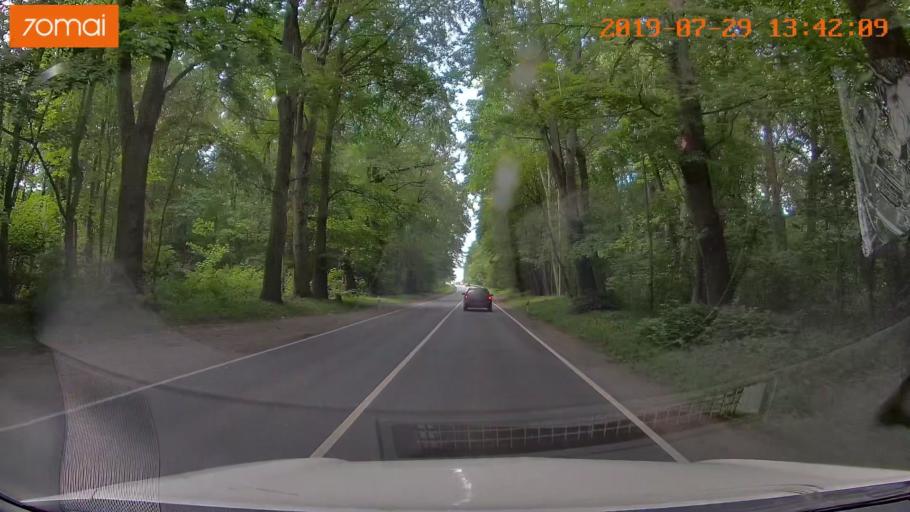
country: RU
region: Kaliningrad
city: Svetlyy
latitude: 54.7365
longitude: 20.1168
